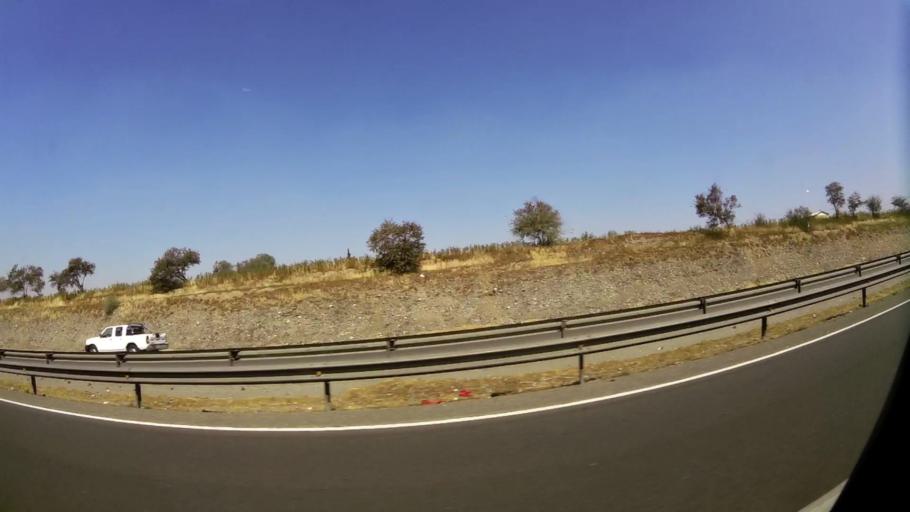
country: CL
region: Santiago Metropolitan
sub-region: Provincia de Santiago
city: Lo Prado
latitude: -33.4839
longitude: -70.7290
